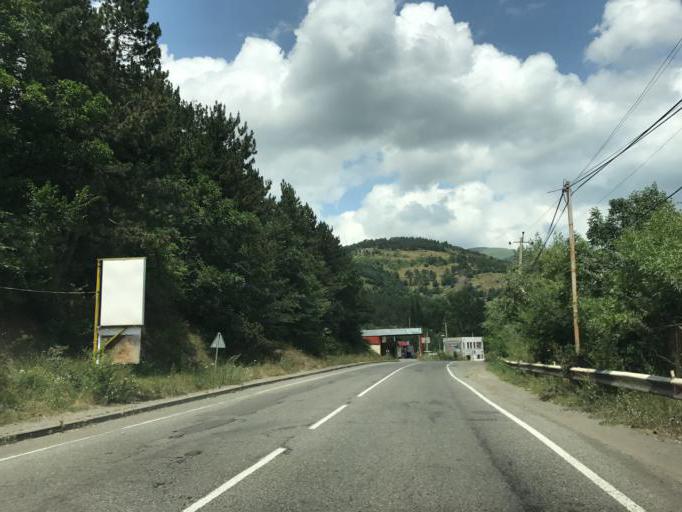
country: AM
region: Tavush
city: Dilijan
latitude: 40.7443
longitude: 44.8681
